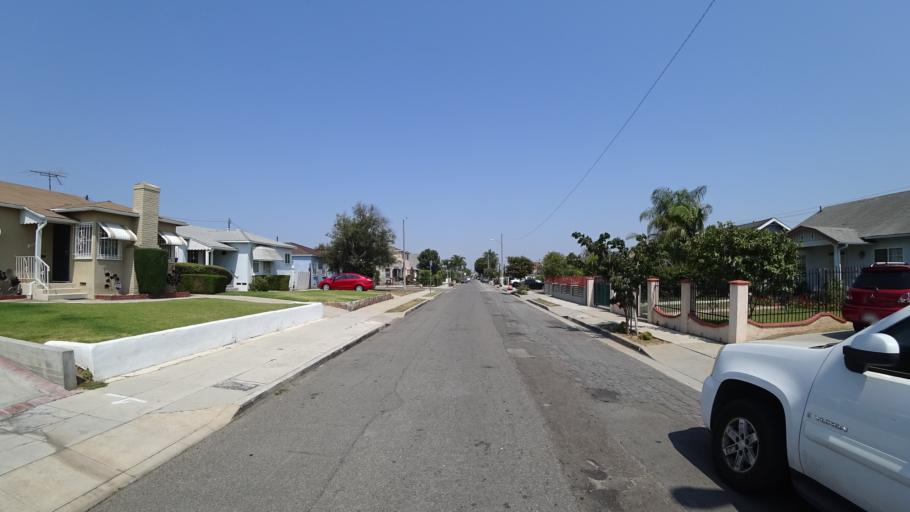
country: US
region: California
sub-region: Los Angeles County
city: View Park-Windsor Hills
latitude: 33.9817
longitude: -118.3433
